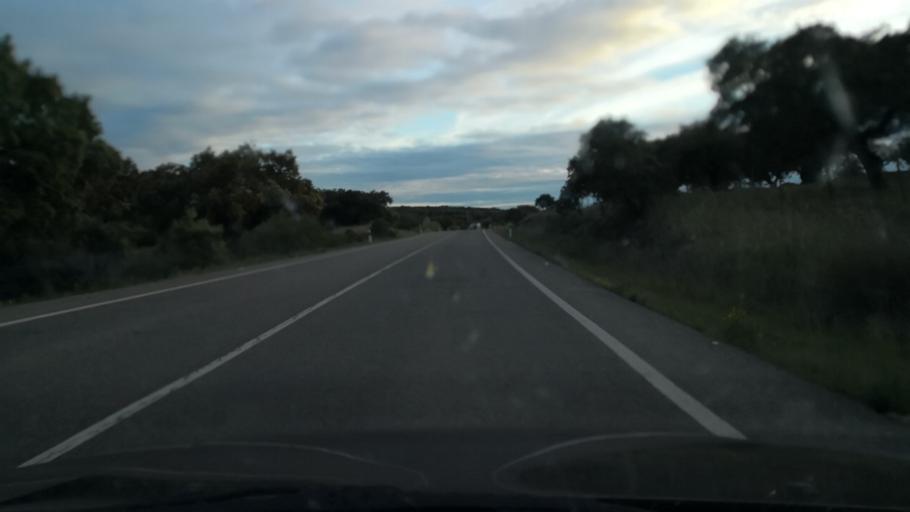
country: ES
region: Extremadura
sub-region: Provincia de Badajoz
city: Puebla de Obando
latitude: 39.1407
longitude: -6.6548
